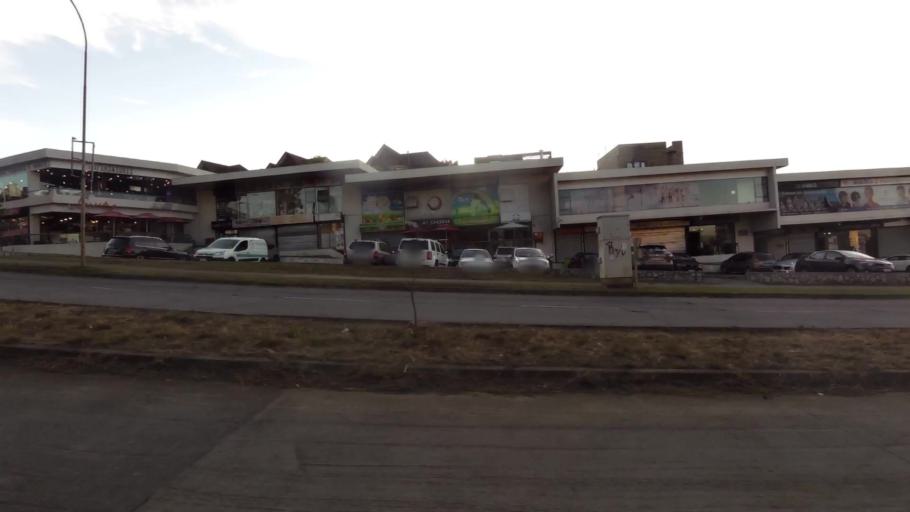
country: CL
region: Biobio
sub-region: Provincia de Concepcion
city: Concepcion
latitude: -36.8479
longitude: -73.0925
